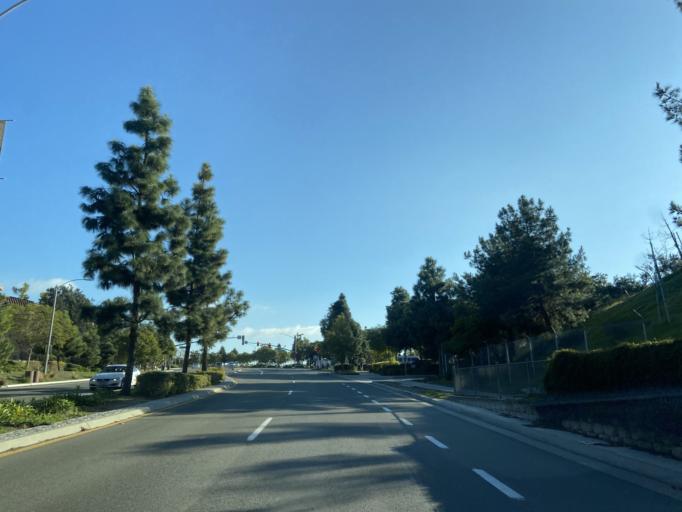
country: US
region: California
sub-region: San Diego County
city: Bonita
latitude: 32.6344
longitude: -116.9676
